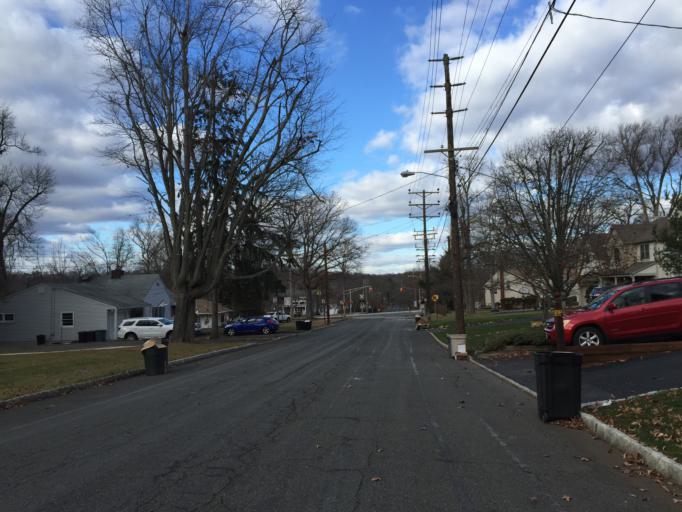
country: US
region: New Jersey
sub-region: Union County
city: New Providence
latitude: 40.6975
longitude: -74.3978
